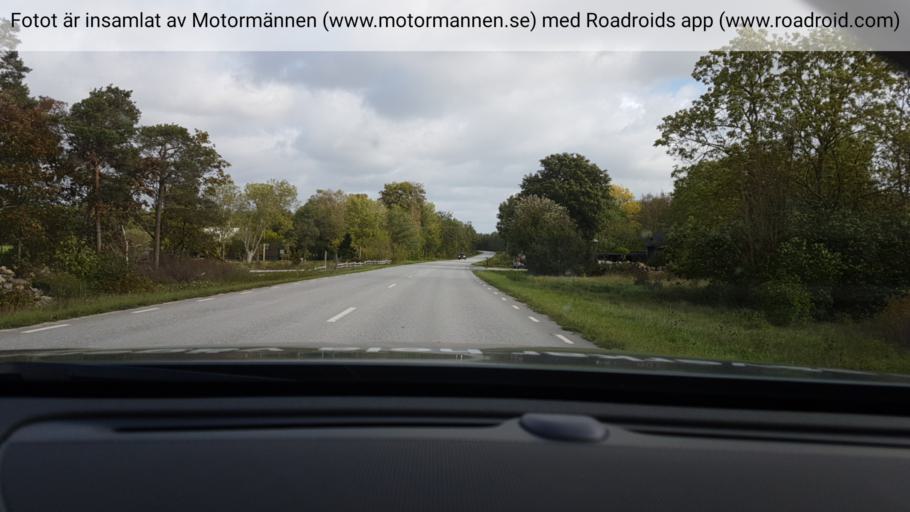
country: SE
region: Gotland
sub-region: Gotland
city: Slite
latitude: 57.7671
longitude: 18.7676
